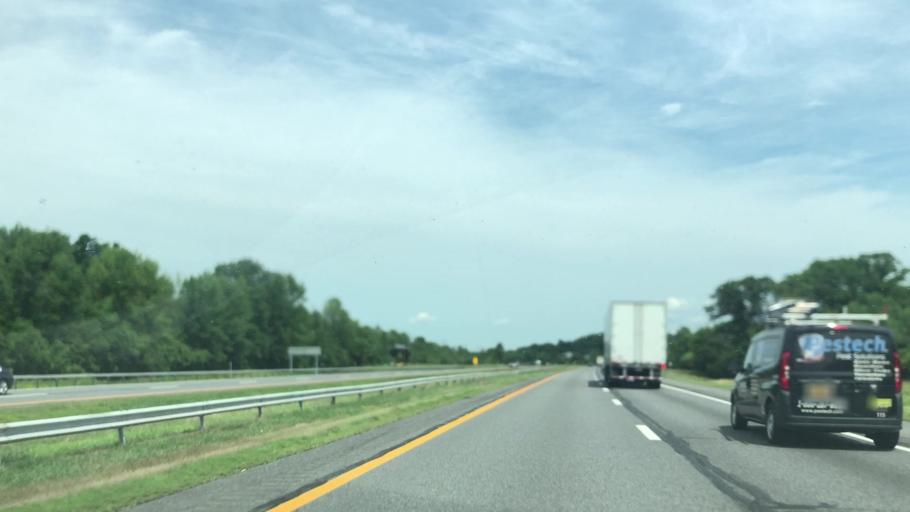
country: US
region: New York
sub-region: Albany County
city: Ravena
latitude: 42.4620
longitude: -73.8078
